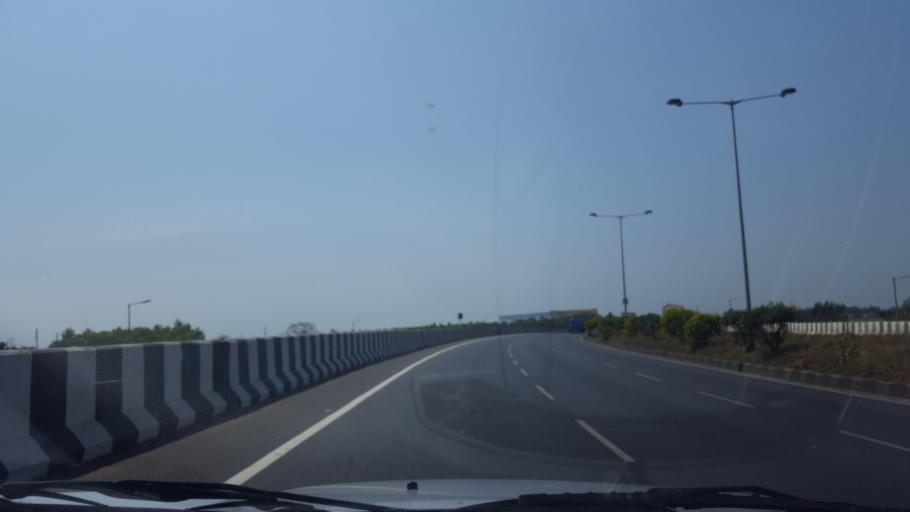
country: IN
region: Andhra Pradesh
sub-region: Prakasam
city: Singarayakonda
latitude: 15.3526
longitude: 80.0386
